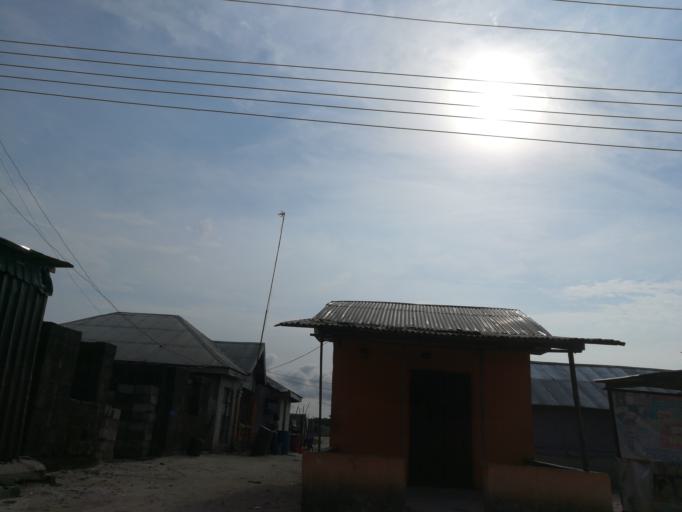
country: NG
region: Rivers
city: Okrika
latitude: 4.7360
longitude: 7.0862
